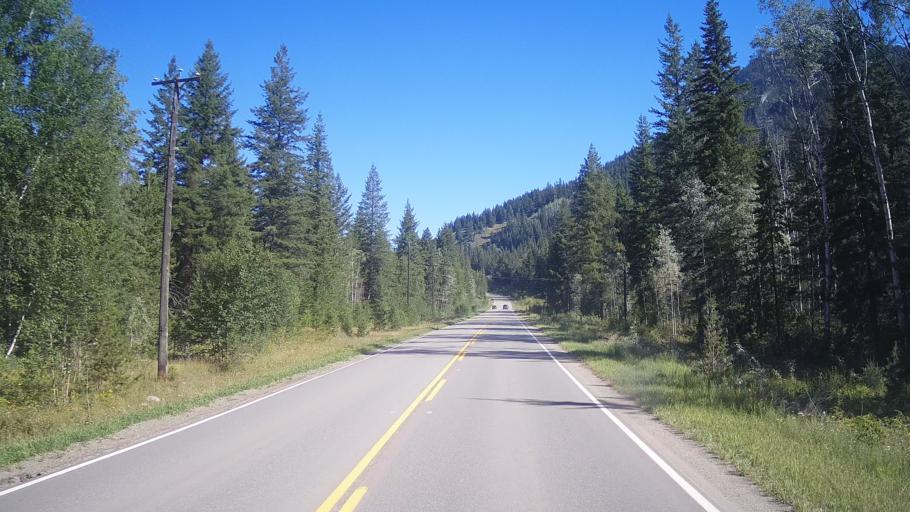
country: CA
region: British Columbia
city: Kamloops
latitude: 51.4422
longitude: -120.2121
